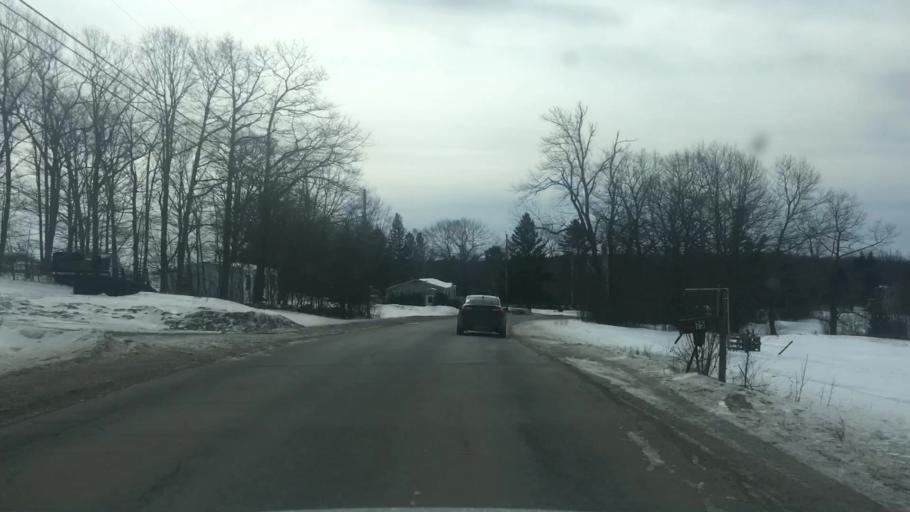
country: US
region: Maine
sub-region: Hancock County
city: Orland
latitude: 44.5773
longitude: -68.7258
